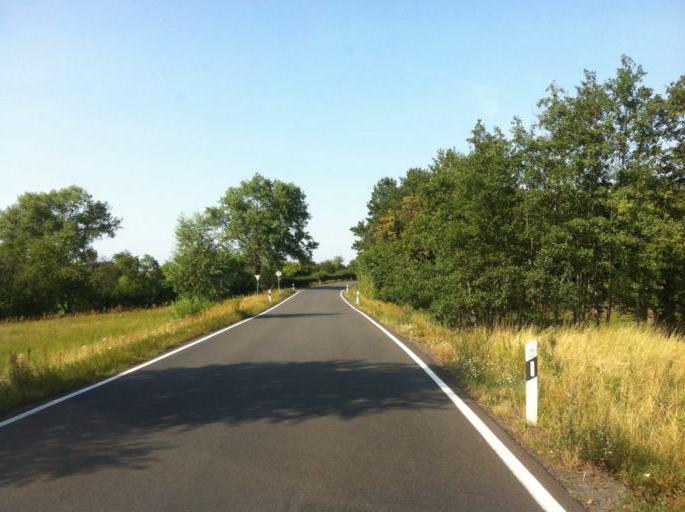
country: DE
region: Saxony
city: Grossbardau
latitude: 51.2115
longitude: 12.7039
